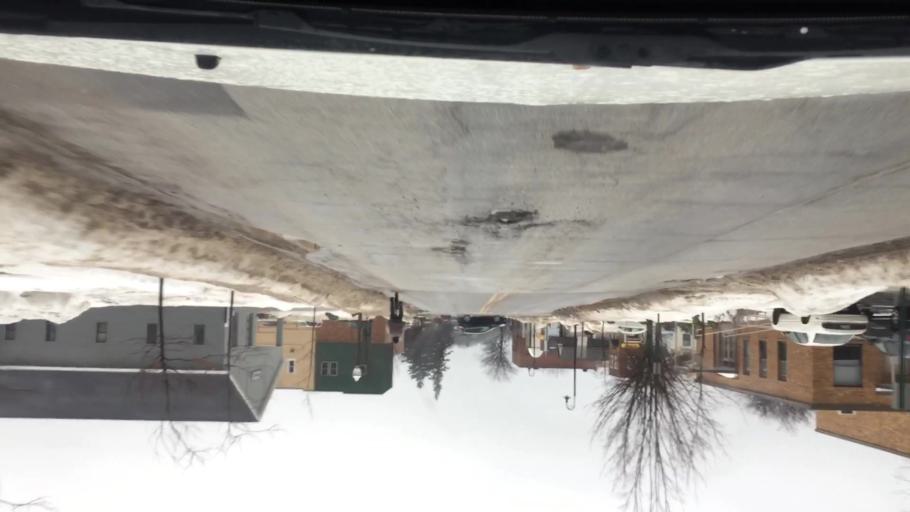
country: US
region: Michigan
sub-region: Charlevoix County
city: Charlevoix
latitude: 45.3152
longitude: -85.2617
